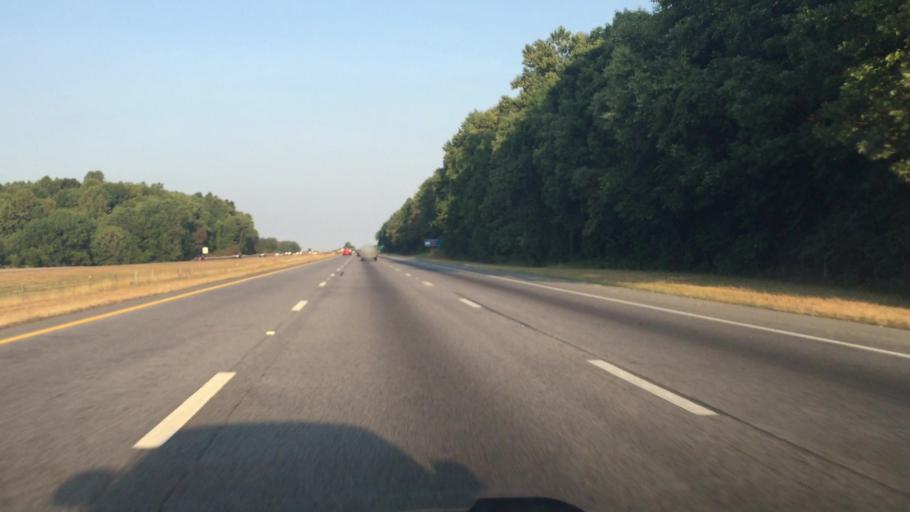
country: US
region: North Carolina
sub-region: Randolph County
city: Trinity
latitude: 35.8681
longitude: -80.0245
